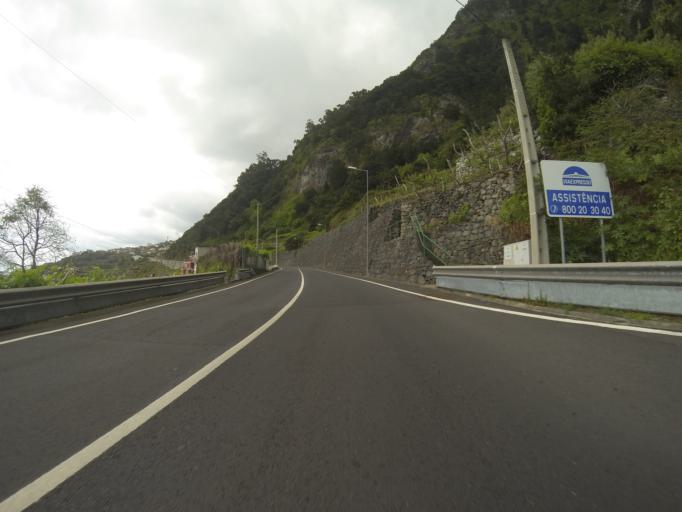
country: PT
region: Madeira
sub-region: Porto Moniz
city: Porto Moniz
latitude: 32.8259
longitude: -17.1195
